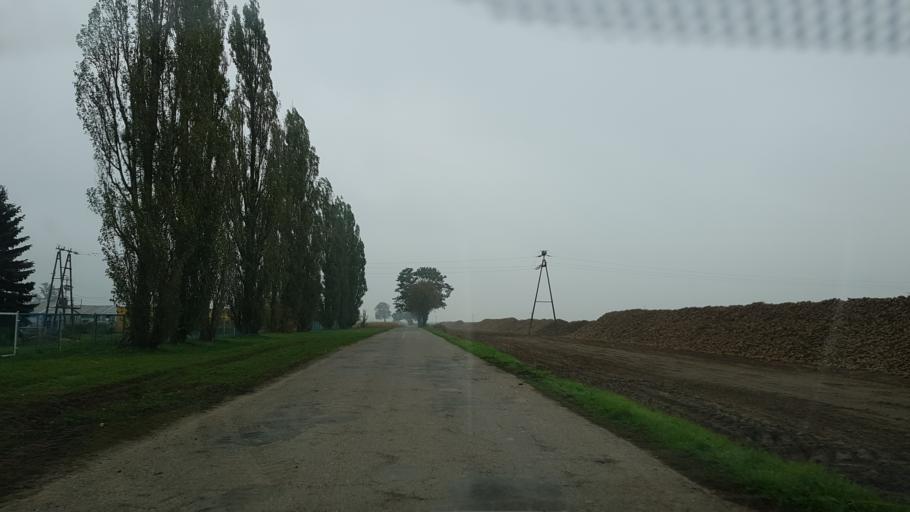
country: PL
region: West Pomeranian Voivodeship
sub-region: Powiat pyrzycki
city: Warnice
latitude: 53.2715
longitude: 15.0371
